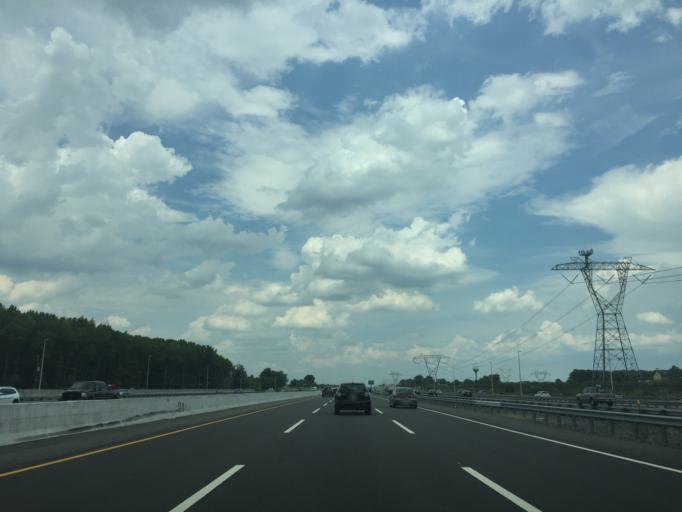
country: US
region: New Jersey
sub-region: Mercer County
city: Yardville
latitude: 40.1716
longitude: -74.6394
